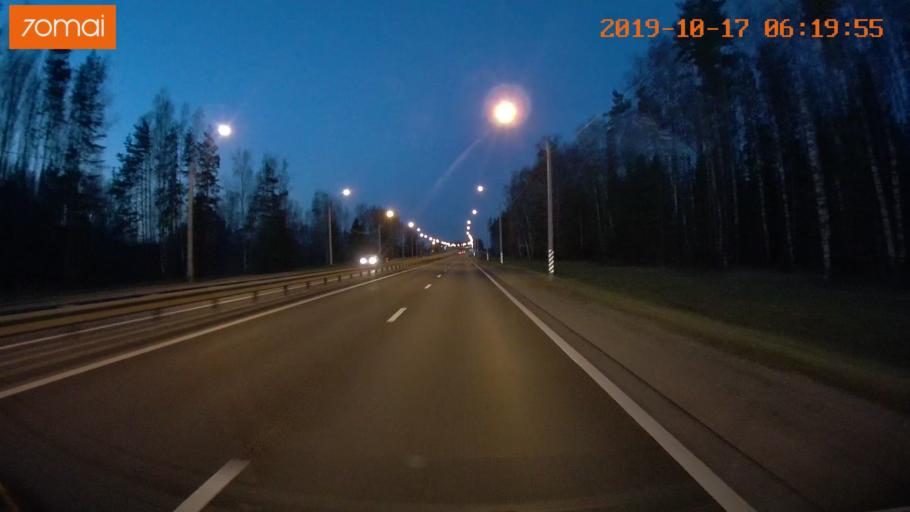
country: RU
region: Ivanovo
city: Lezhnevo
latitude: 56.8224
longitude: 40.8941
